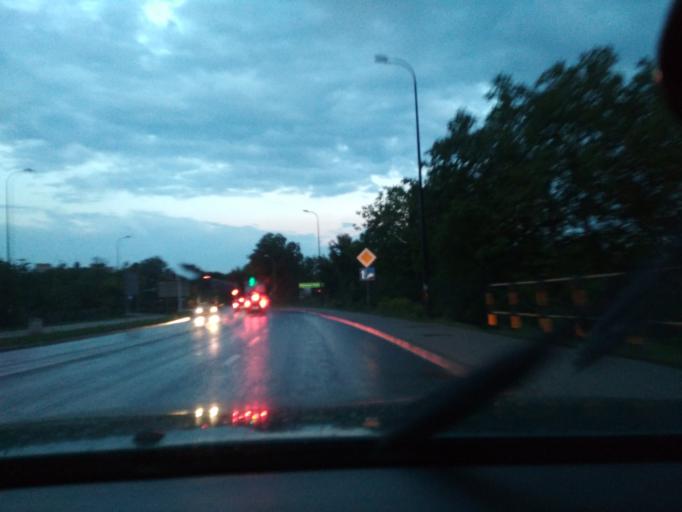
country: PL
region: Silesian Voivodeship
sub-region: Gliwice
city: Gliwice
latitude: 50.3027
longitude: 18.6589
